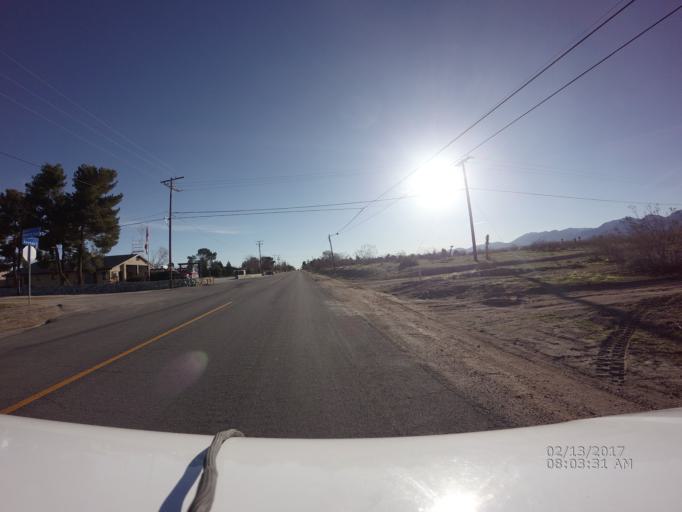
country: US
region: California
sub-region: Los Angeles County
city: Littlerock
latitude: 34.5284
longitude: -117.9714
